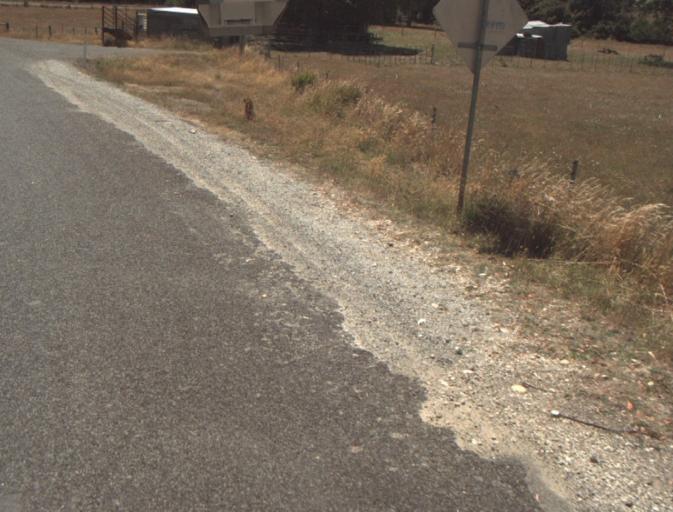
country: AU
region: Tasmania
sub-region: Dorset
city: Scottsdale
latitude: -41.3122
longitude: 147.3759
